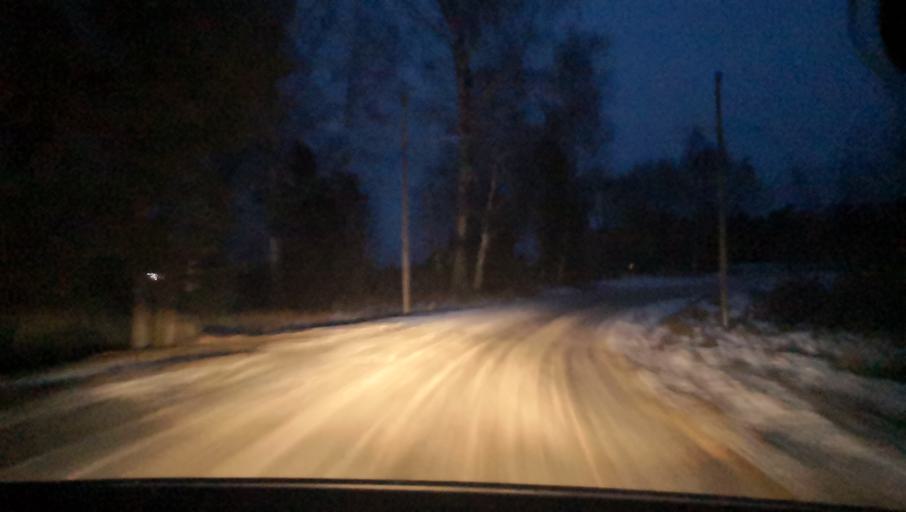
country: SE
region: Uppsala
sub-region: Heby Kommun
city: Tarnsjo
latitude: 60.2629
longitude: 16.7874
